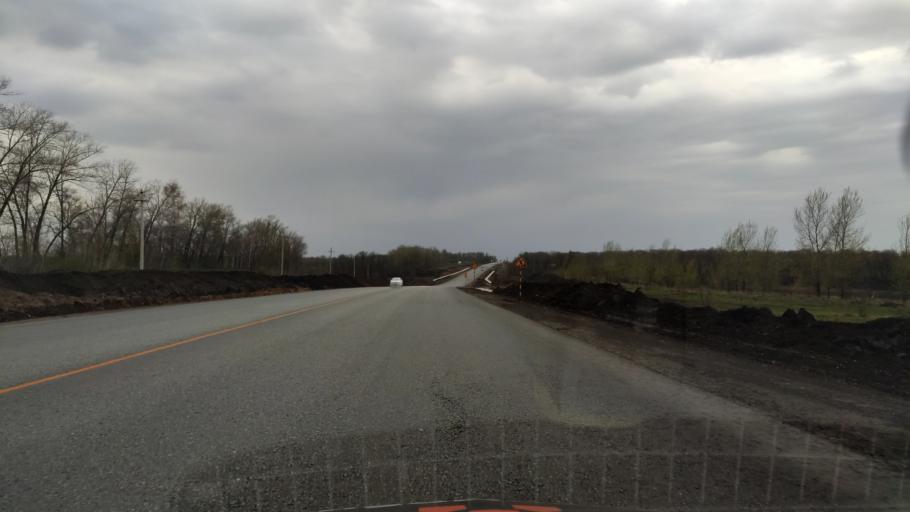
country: RU
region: Kursk
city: Gorshechnoye
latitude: 51.5480
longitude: 38.0562
